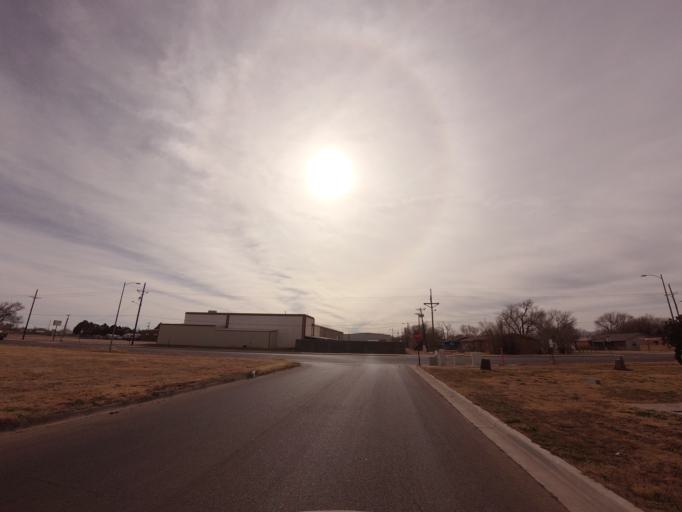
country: US
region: New Mexico
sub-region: Curry County
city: Clovis
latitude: 34.4050
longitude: -103.2405
